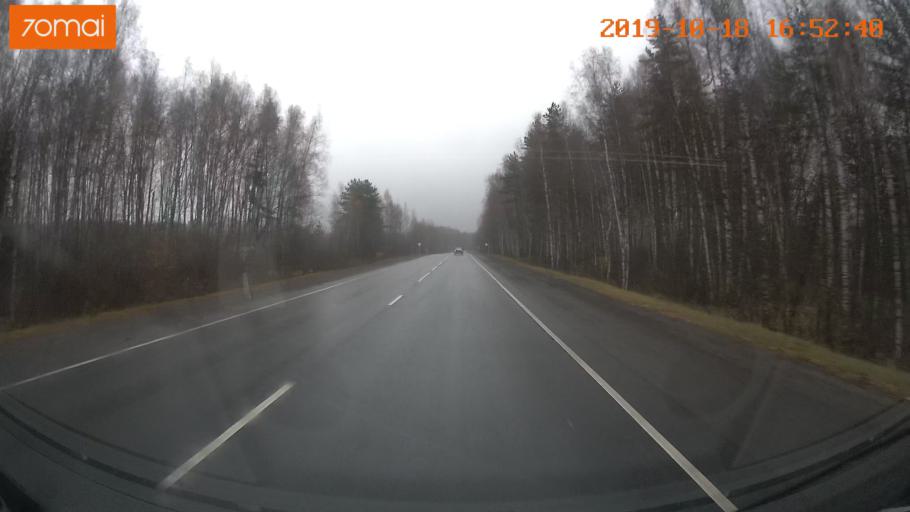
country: RU
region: Ivanovo
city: Nerl'
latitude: 56.6040
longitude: 40.5561
